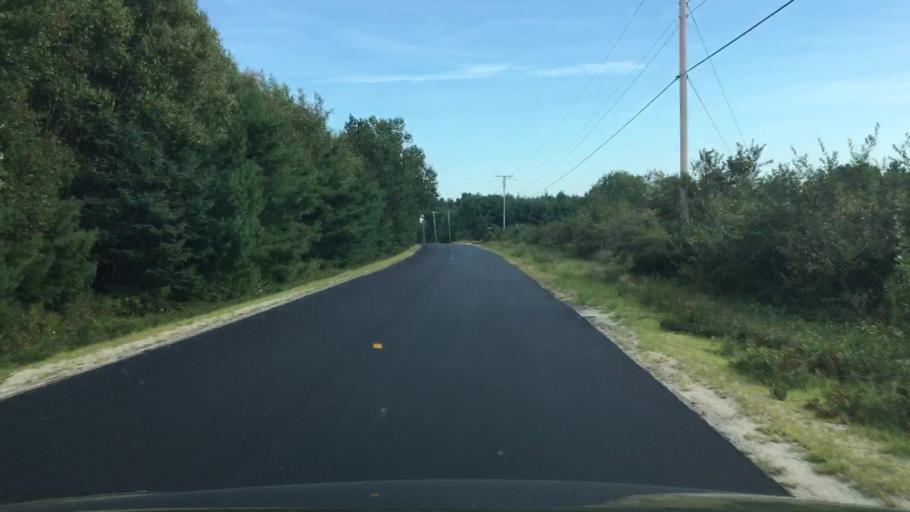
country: US
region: Maine
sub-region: Hancock County
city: Surry
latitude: 44.5312
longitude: -68.6130
